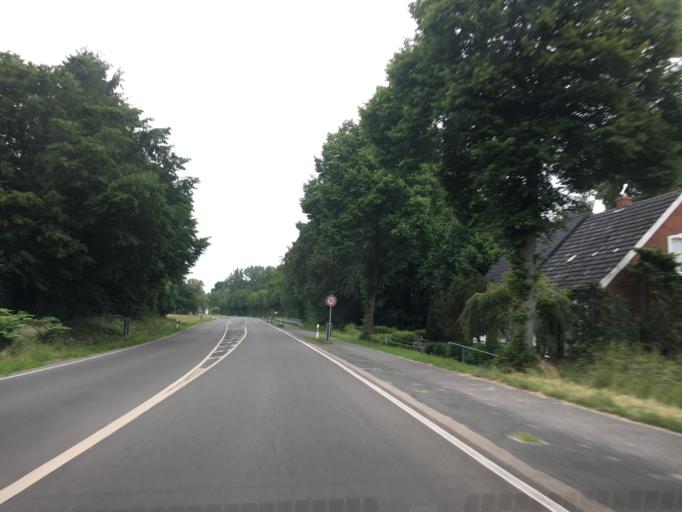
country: DE
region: North Rhine-Westphalia
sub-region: Regierungsbezirk Munster
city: Steinfurt
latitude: 52.1370
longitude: 7.3437
